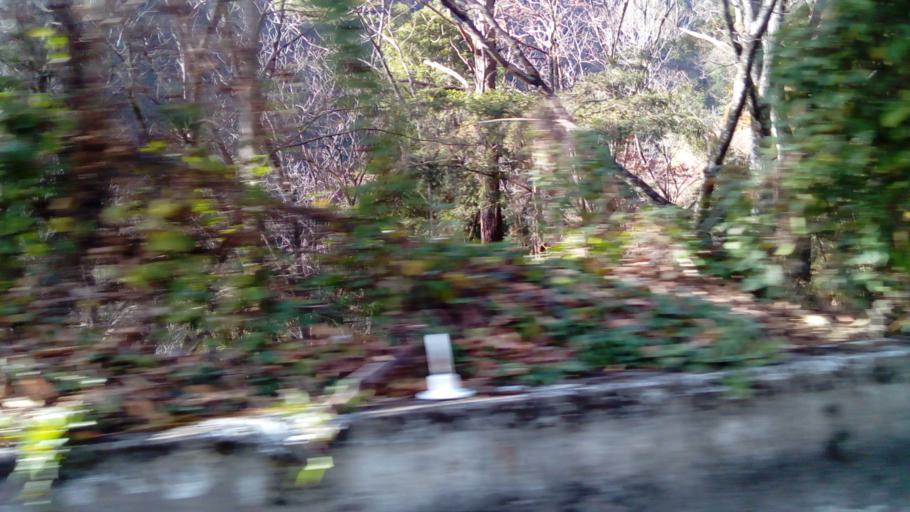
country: TW
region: Taiwan
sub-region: Hualien
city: Hualian
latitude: 24.3452
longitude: 121.3159
